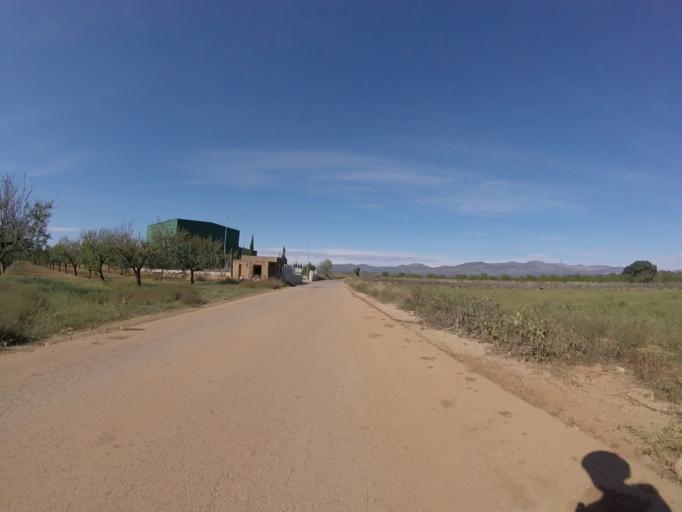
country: ES
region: Valencia
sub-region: Provincia de Castello
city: Benlloch
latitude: 40.2061
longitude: 0.0485
